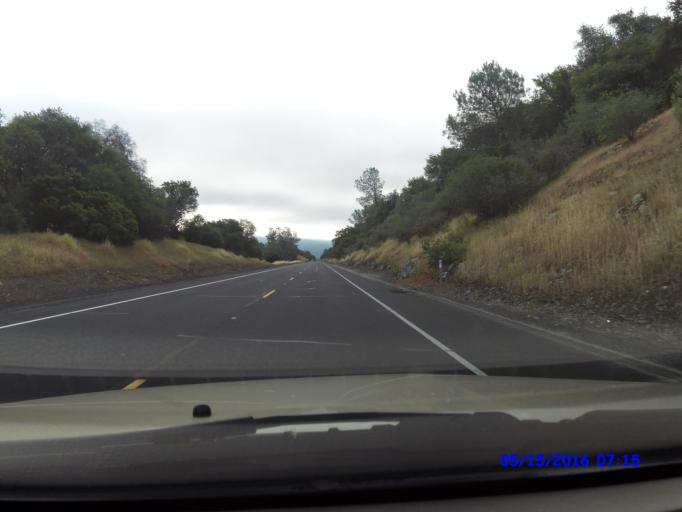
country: US
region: California
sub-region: Tuolumne County
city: Jamestown
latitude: 37.8278
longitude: -120.3422
